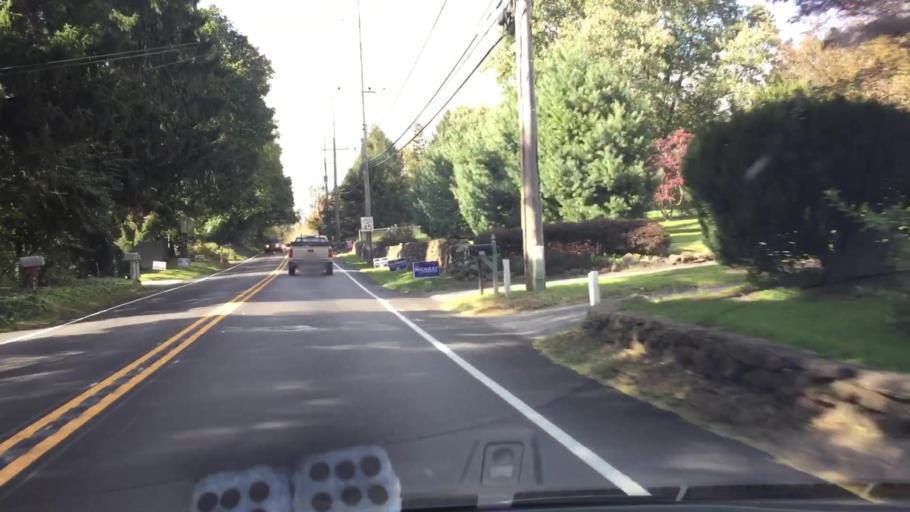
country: US
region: Pennsylvania
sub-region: Chester County
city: Malvern
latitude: 39.9695
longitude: -75.5276
